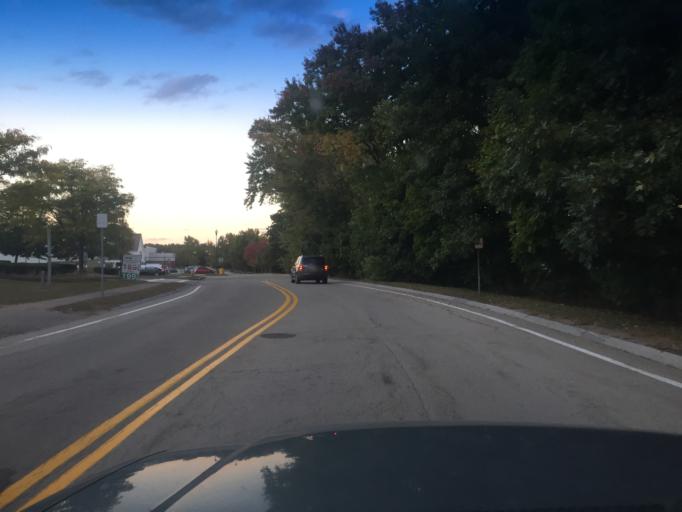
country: US
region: Massachusetts
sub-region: Norfolk County
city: Franklin
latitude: 42.0920
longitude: -71.4342
